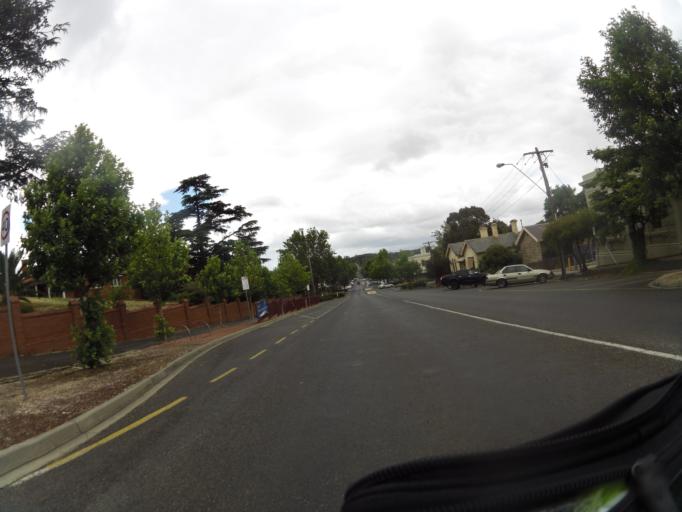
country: AU
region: Victoria
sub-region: Mount Alexander
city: Castlemaine
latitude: -37.0639
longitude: 144.2197
